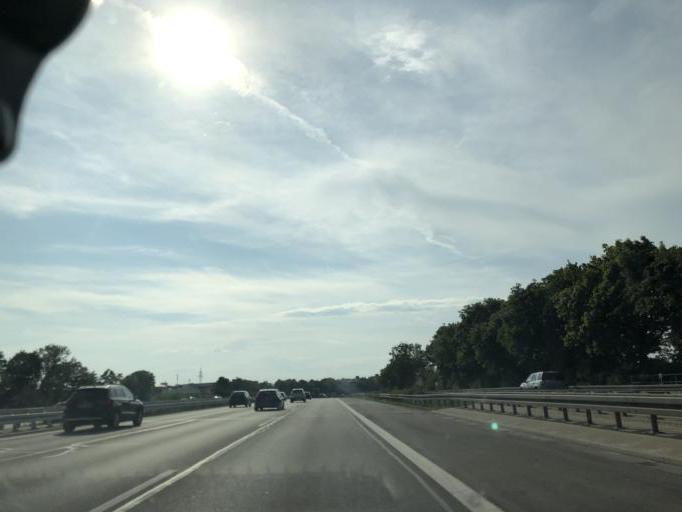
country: DE
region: Bavaria
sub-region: Upper Bavaria
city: Pasing
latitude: 48.1248
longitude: 11.4570
